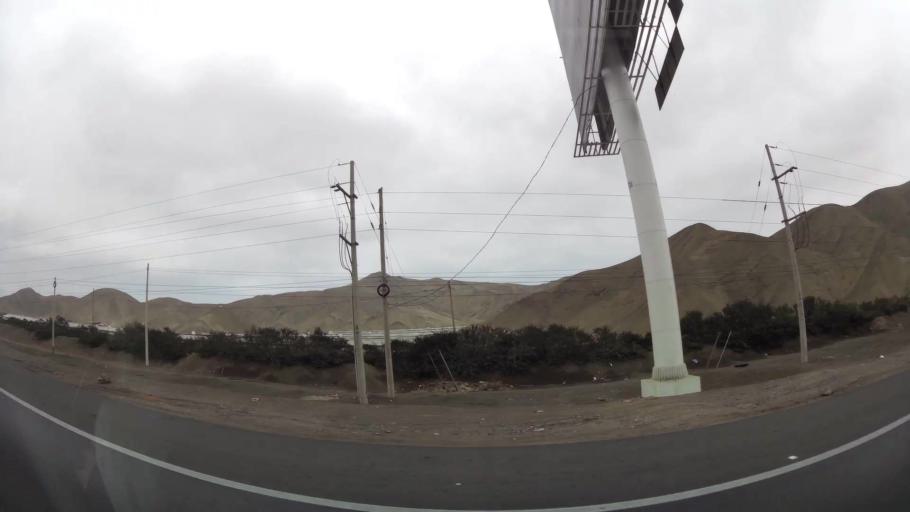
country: PE
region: Lima
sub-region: Lima
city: San Bartolo
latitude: -12.4087
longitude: -76.7567
